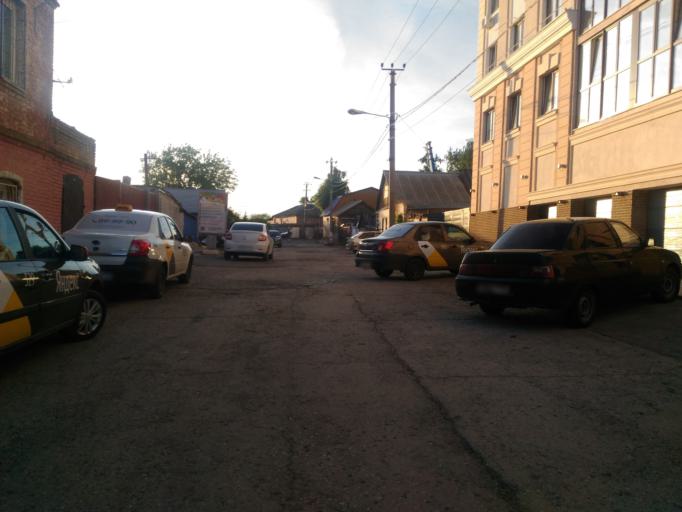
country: RU
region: Ulyanovsk
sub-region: Ulyanovskiy Rayon
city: Ulyanovsk
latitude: 54.3173
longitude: 48.3794
